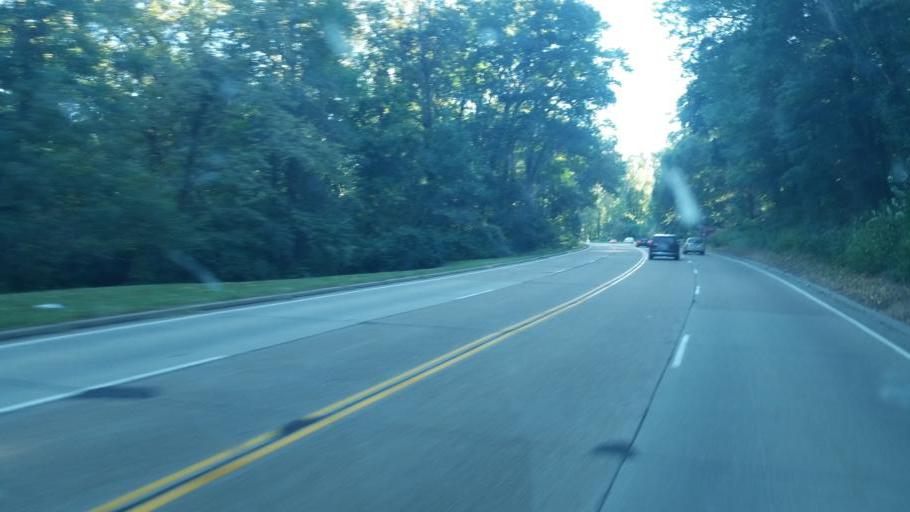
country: US
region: Virginia
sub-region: Fairfax County
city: Fort Hunt
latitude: 38.7539
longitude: -77.0501
